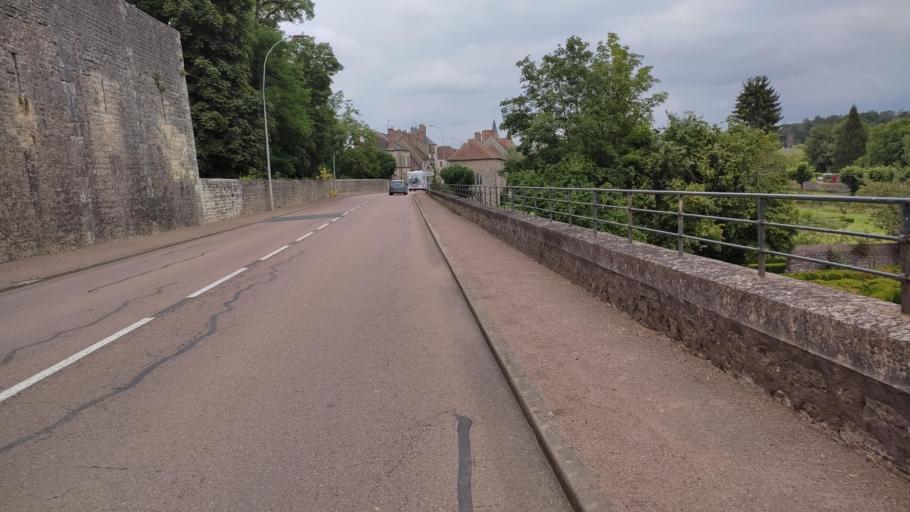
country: FR
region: Bourgogne
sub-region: Departement de la Nievre
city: Chatillon-en-Bazois
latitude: 47.0499
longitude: 3.6520
